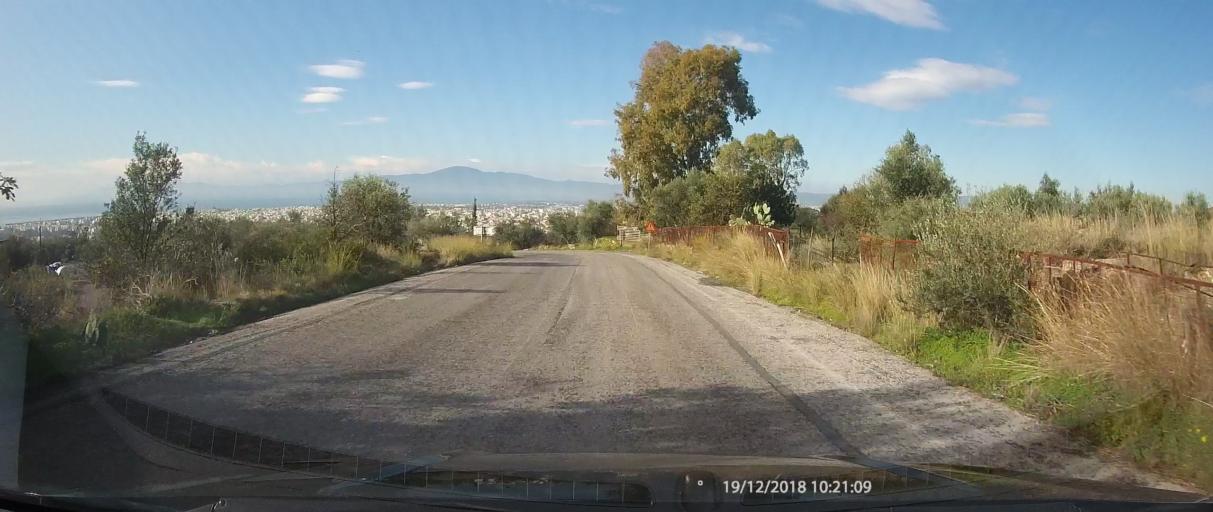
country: GR
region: Peloponnese
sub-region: Nomos Messinias
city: Kalamata
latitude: 37.0482
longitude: 22.1345
